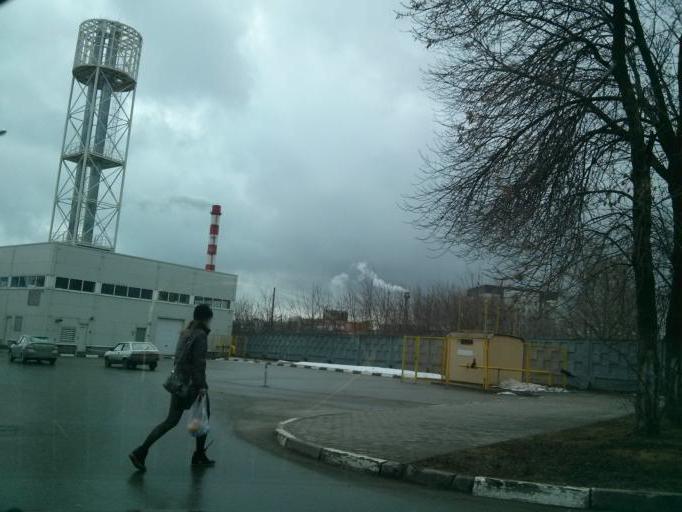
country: RU
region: Nizjnij Novgorod
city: Bor
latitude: 56.3081
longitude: 44.0715
